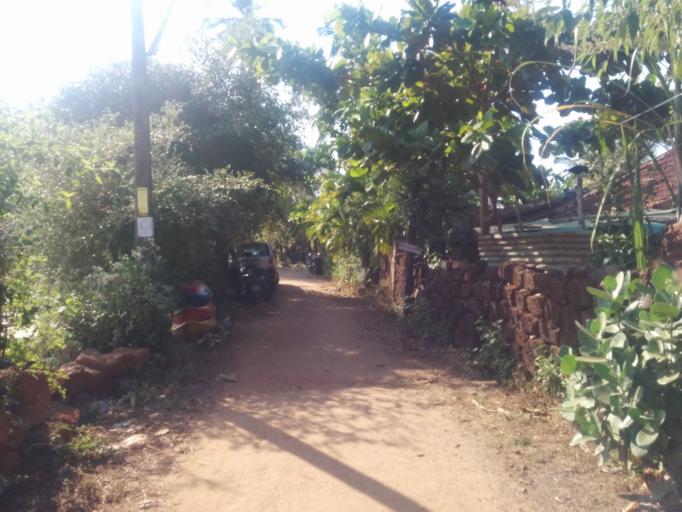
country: IN
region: Karnataka
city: Canacona
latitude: 14.9998
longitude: 74.0297
